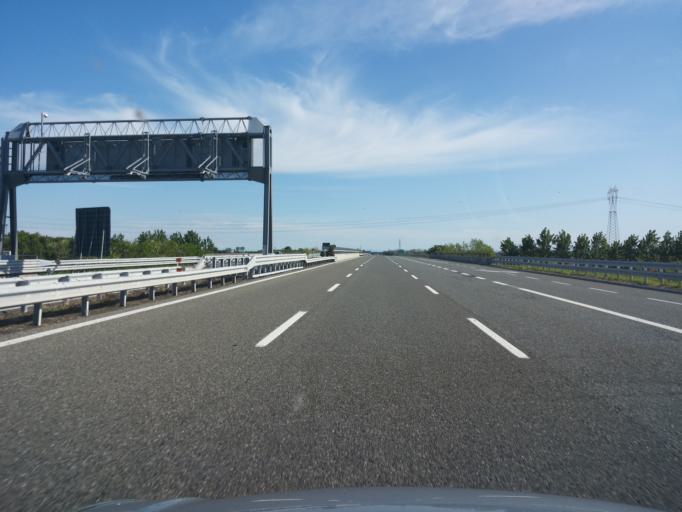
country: IT
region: Piedmont
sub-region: Provincia di Novara
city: Biandrate
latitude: 45.4581
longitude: 8.4529
